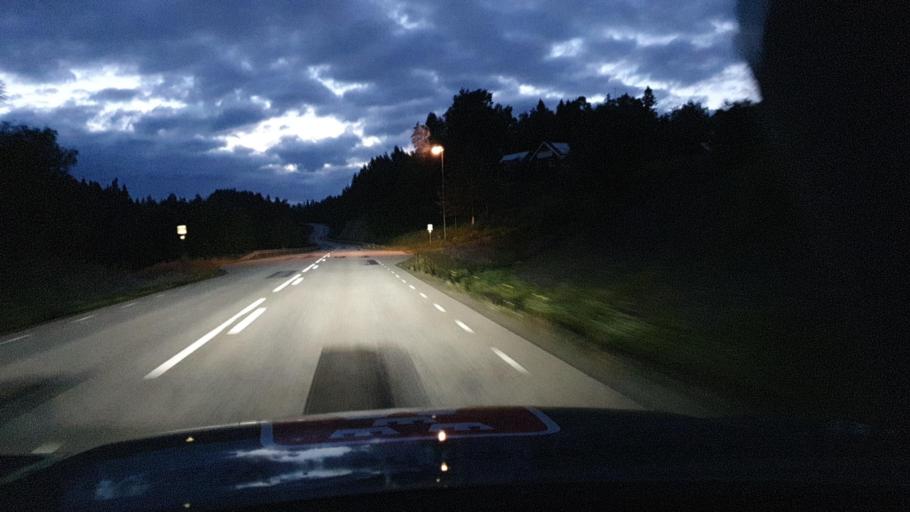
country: SE
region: OErebro
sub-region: Karlskoga Kommun
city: Karlskoga
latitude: 59.4580
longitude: 14.5032
